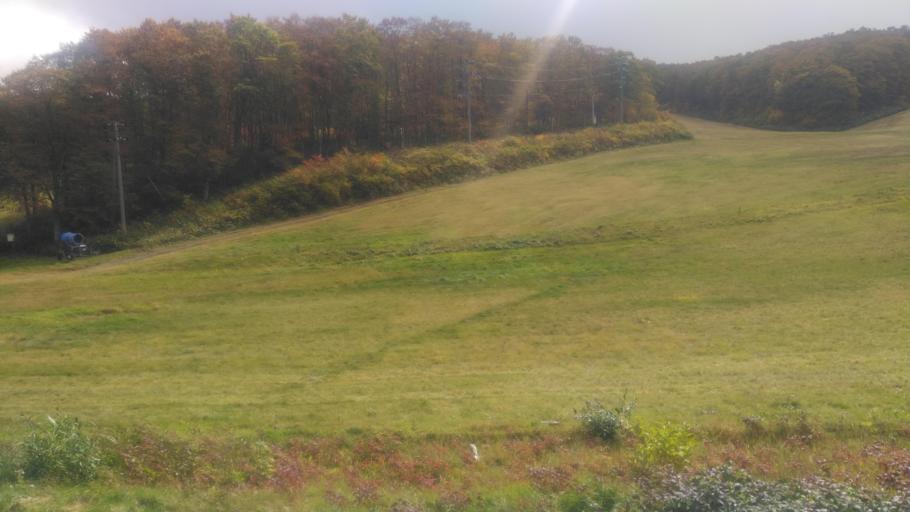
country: JP
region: Yamagata
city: Yamagata-shi
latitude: 38.1677
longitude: 140.4184
